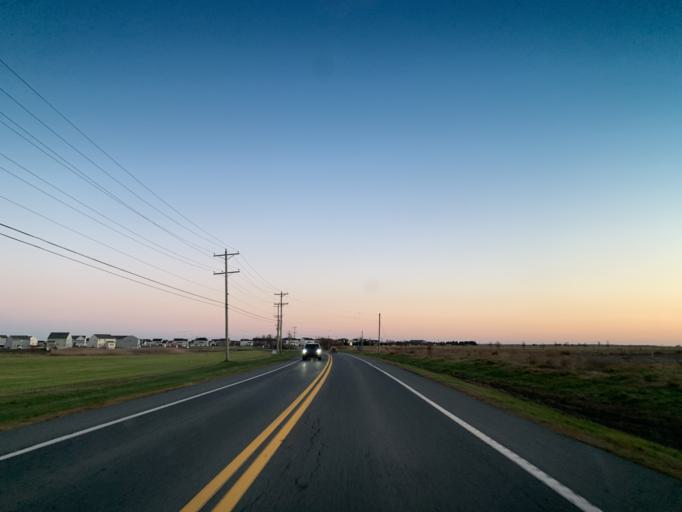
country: US
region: Delaware
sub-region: New Castle County
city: Middletown
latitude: 39.4323
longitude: -75.7430
